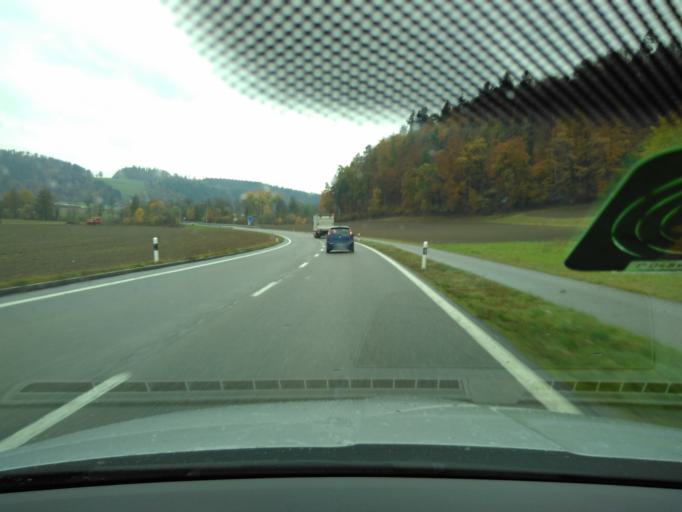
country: CH
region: Aargau
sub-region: Bezirk Kulm
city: Schoftland
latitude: 47.2930
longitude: 8.0516
